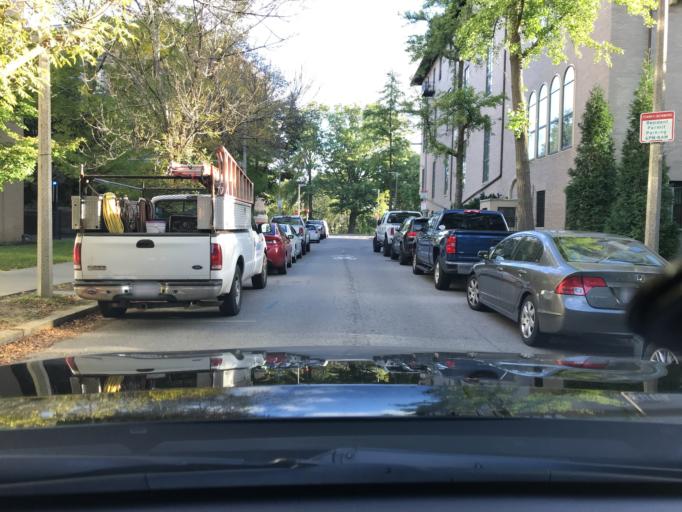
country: US
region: Massachusetts
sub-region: Norfolk County
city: Brookline
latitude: 42.3383
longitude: -71.0995
